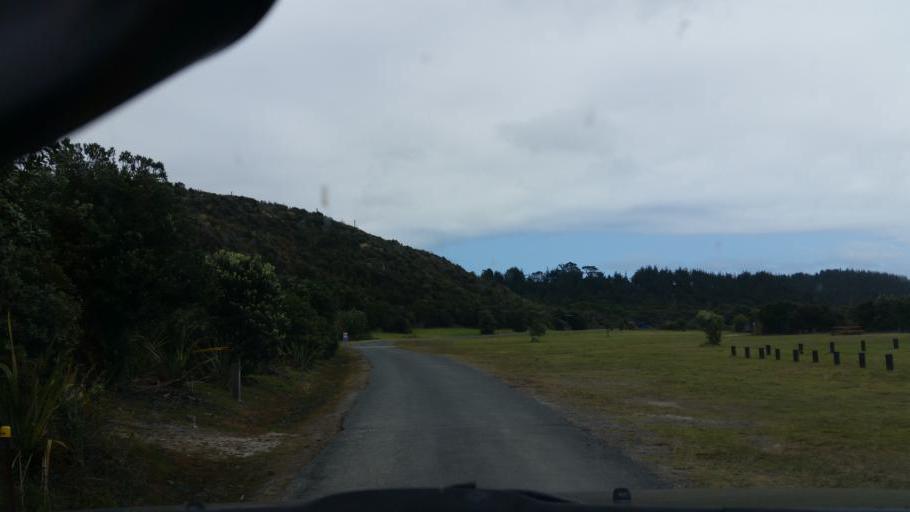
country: NZ
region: Northland
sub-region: Kaipara District
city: Dargaville
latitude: -35.8094
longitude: 173.6626
